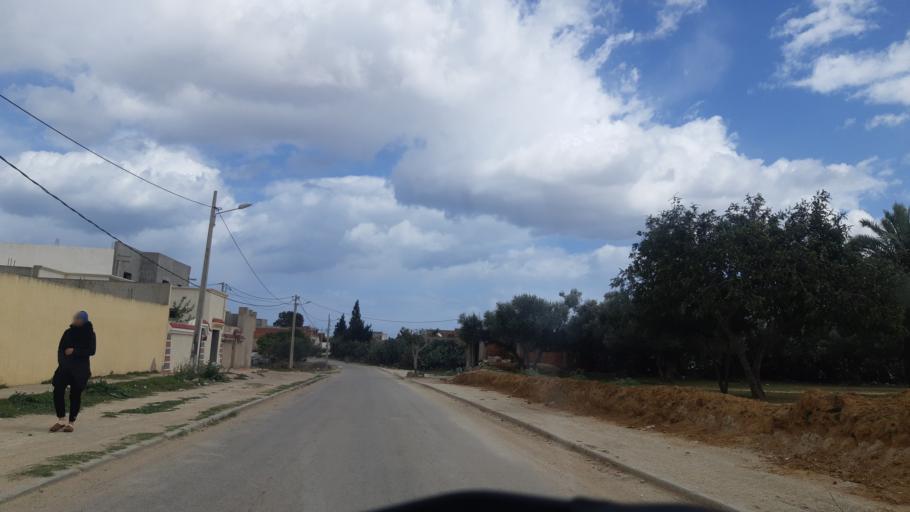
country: TN
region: Susah
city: Akouda
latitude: 35.8625
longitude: 10.5295
